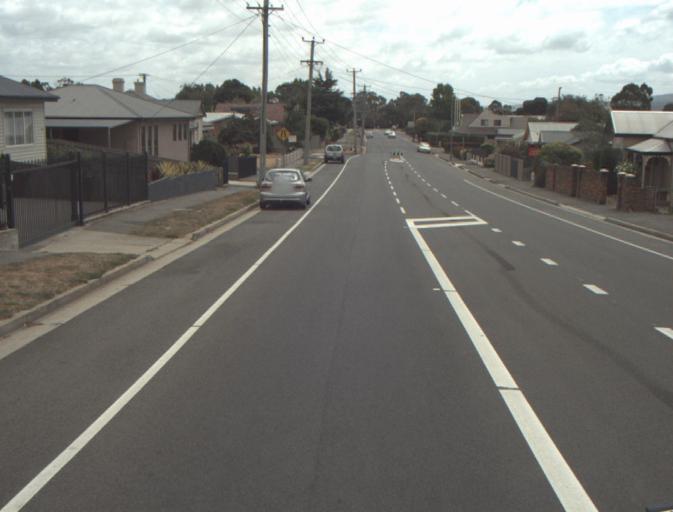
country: AU
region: Tasmania
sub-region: Launceston
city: Newstead
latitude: -41.4568
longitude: 147.1788
